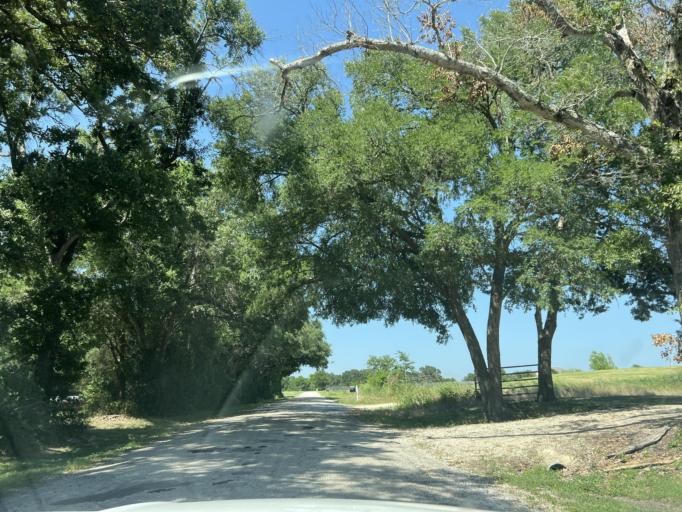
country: US
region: Texas
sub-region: Washington County
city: Brenham
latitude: 30.1754
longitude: -96.4970
